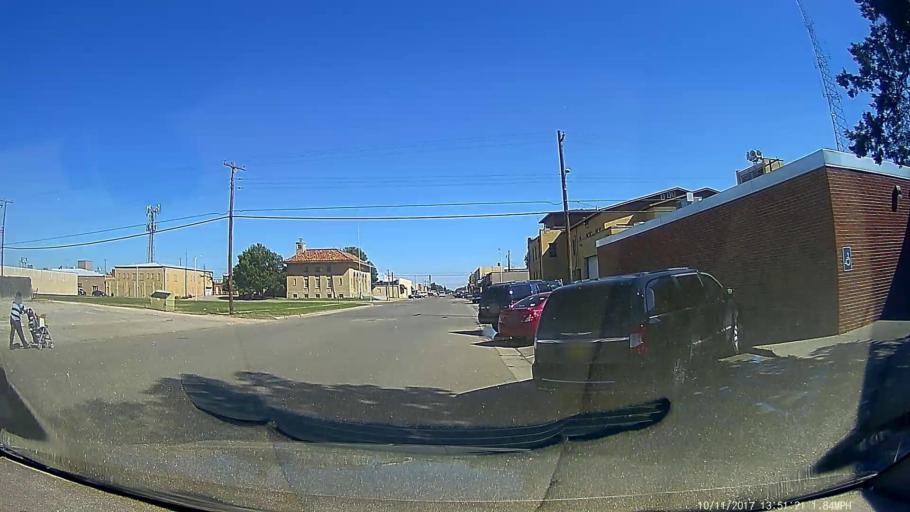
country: US
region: New Mexico
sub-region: Curry County
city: Clovis
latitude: 34.4018
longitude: -103.2071
